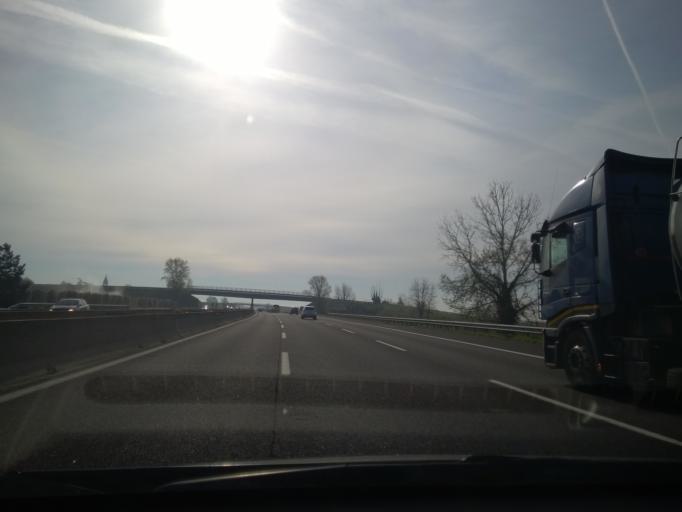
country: IT
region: Emilia-Romagna
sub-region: Provincia di Bologna
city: Mordano
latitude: 44.3613
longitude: 11.7920
